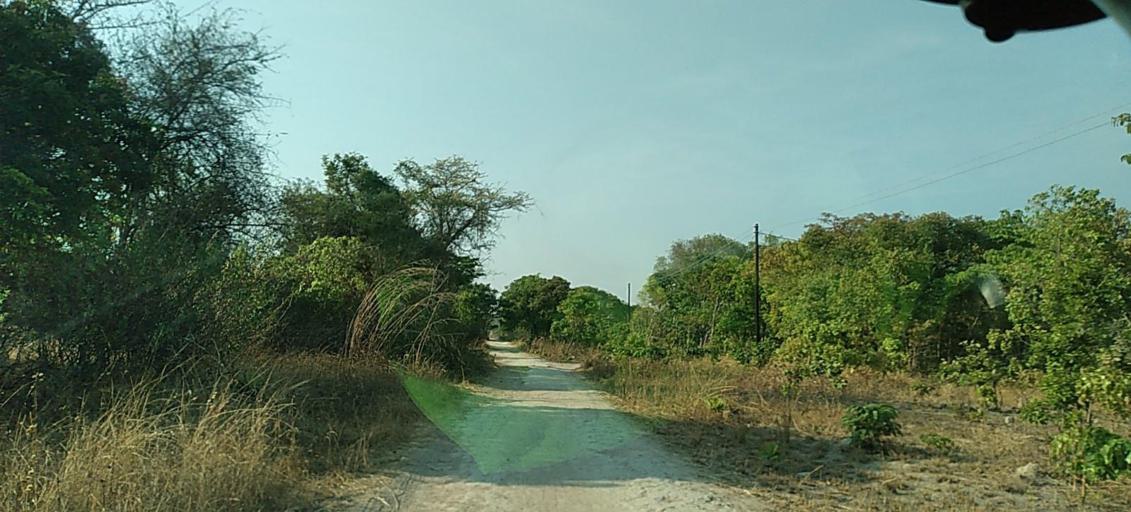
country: ZM
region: North-Western
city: Kalengwa
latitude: -13.1605
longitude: 25.0344
